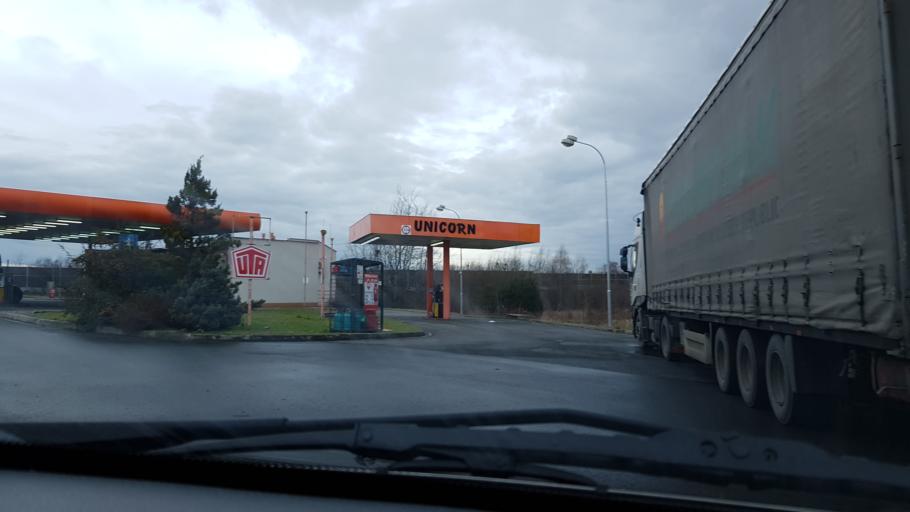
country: CZ
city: Dobra
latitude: 49.6719
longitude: 18.4272
